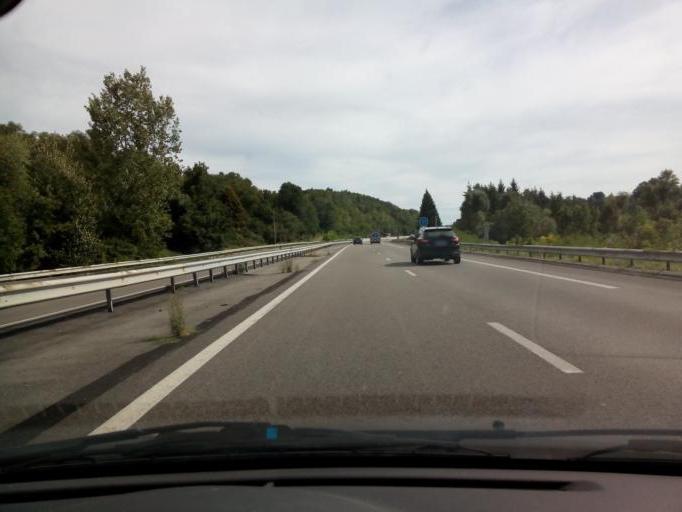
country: FR
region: Rhone-Alpes
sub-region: Departement de l'Isere
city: Chabons
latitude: 45.4707
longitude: 5.4004
